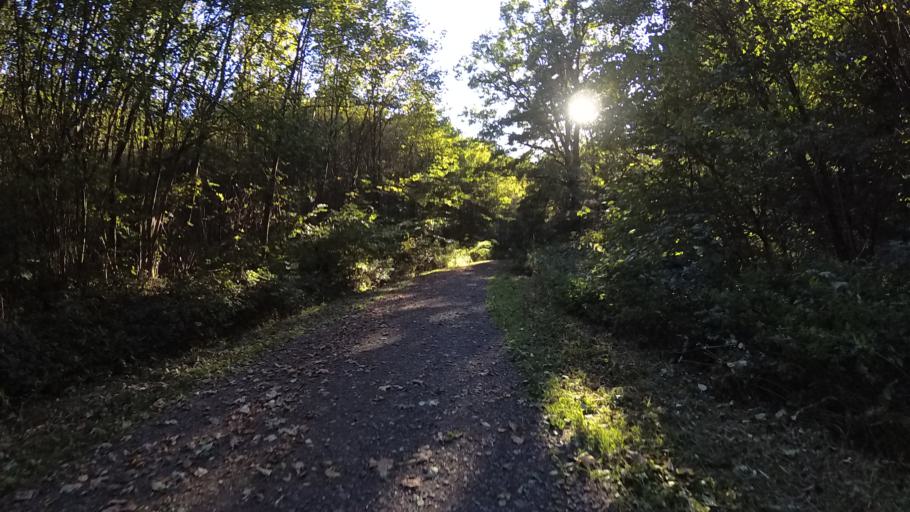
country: DE
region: Saarland
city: Sankt Wendel
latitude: 49.4389
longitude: 7.1876
